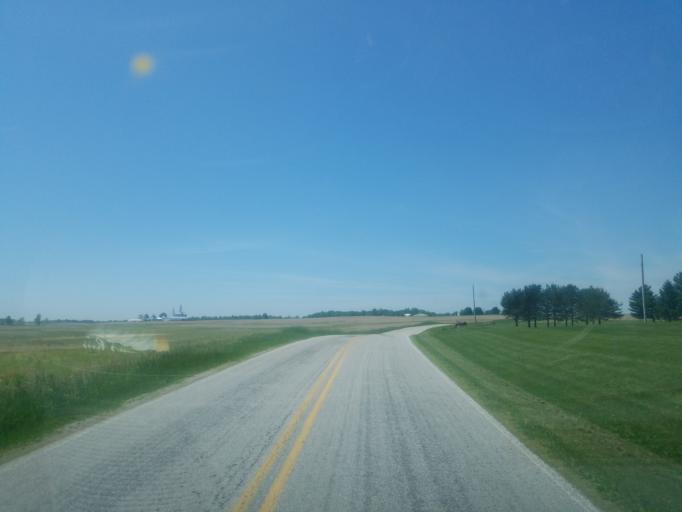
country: US
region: Ohio
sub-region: Huron County
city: New London
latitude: 41.1112
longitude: -82.4503
